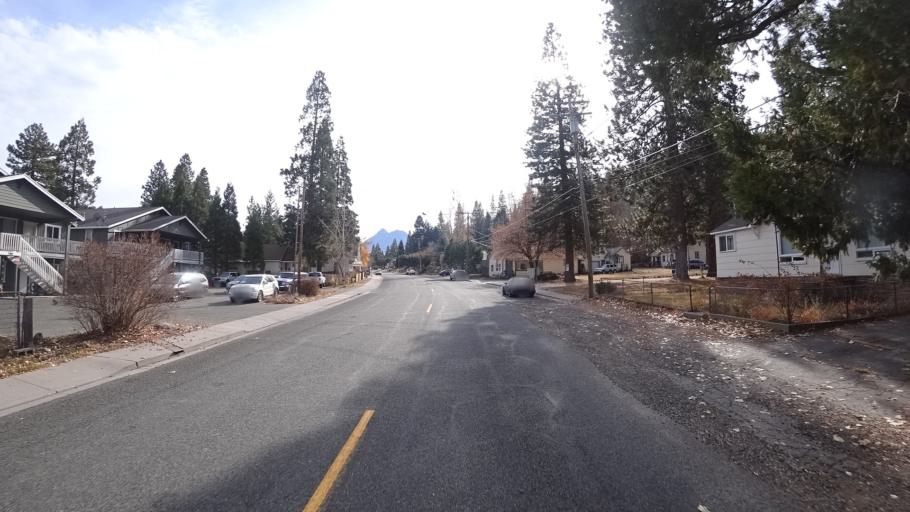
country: US
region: California
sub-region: Siskiyou County
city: Weed
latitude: 41.4130
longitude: -122.3833
